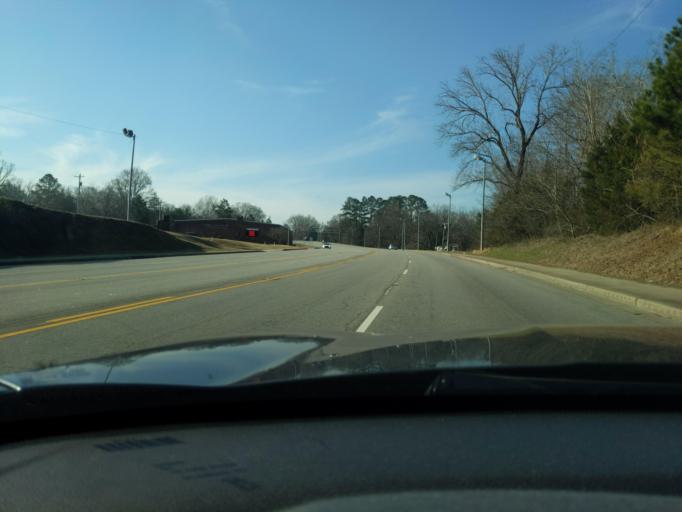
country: US
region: South Carolina
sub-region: Abbeville County
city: Abbeville
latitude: 34.1703
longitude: -82.3794
